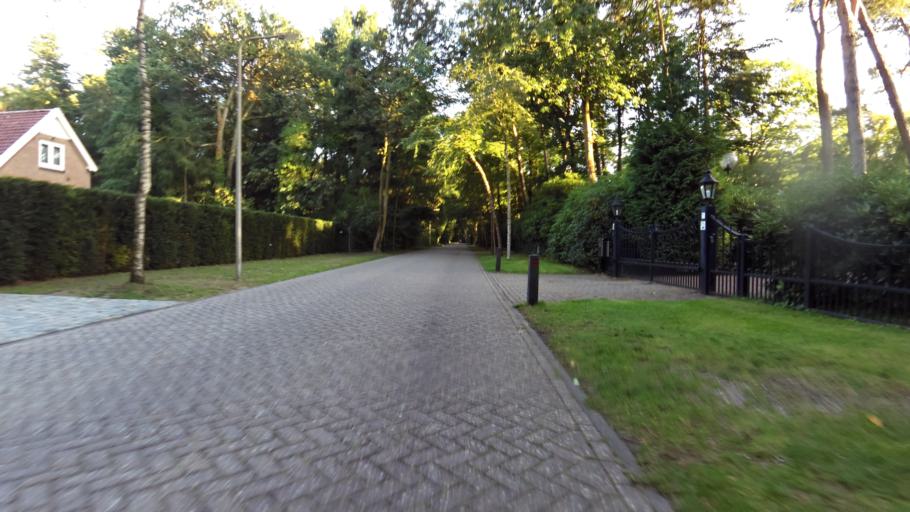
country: NL
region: Utrecht
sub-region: Gemeente Zeist
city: Zeist
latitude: 52.1258
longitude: 5.2460
